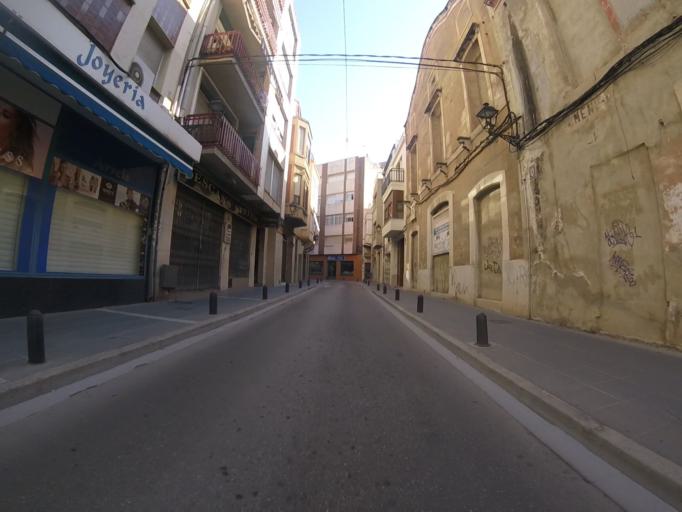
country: ES
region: Valencia
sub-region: Provincia de Castello
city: Benicarlo
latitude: 40.4191
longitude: 0.4259
